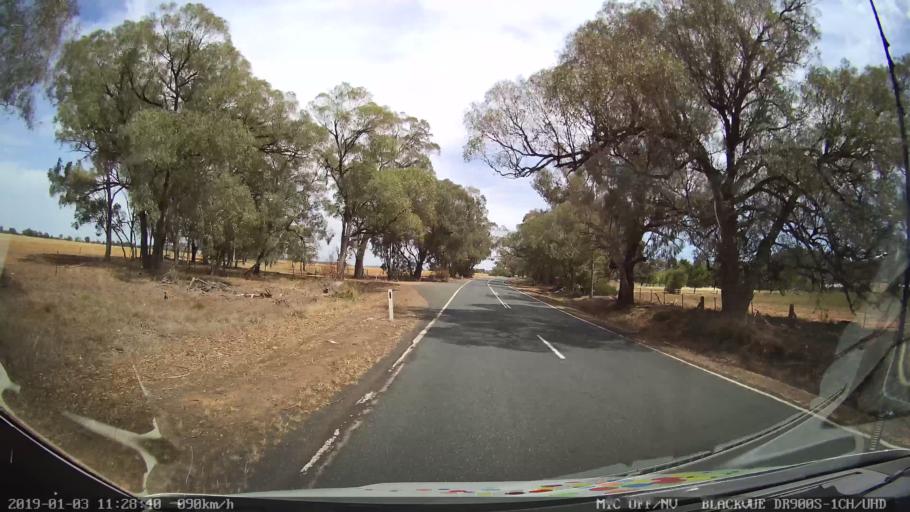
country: AU
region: New South Wales
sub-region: Weddin
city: Grenfell
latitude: -34.0002
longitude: 148.2061
